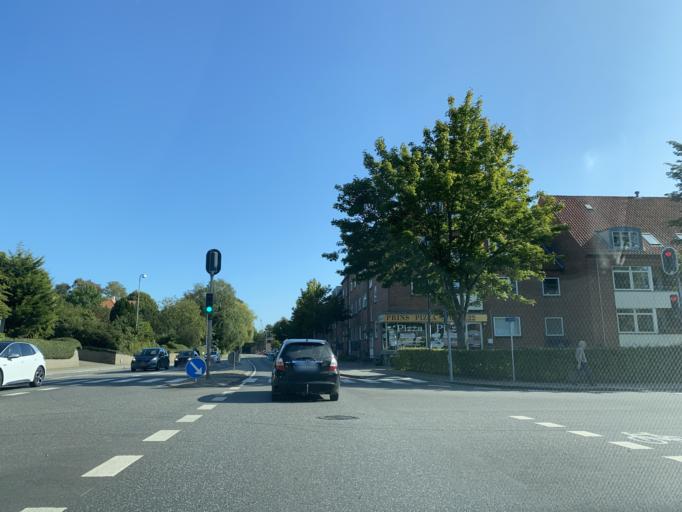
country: DK
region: South Denmark
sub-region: Aabenraa Kommune
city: Aabenraa
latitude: 55.0511
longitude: 9.4123
